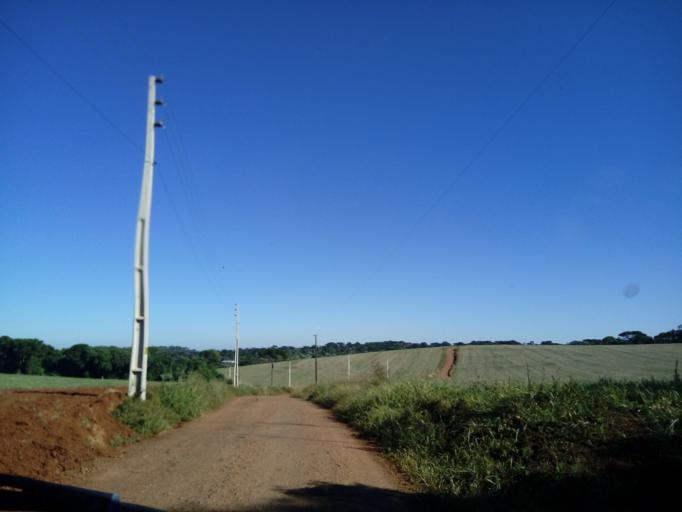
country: BR
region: Santa Catarina
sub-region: Chapeco
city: Chapeco
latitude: -27.2024
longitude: -52.7004
